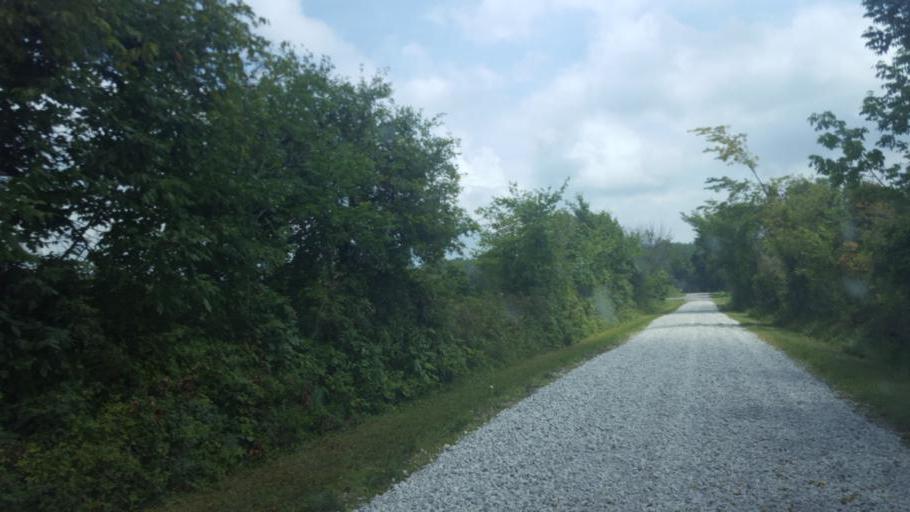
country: US
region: Ohio
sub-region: Morrow County
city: Mount Gilead
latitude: 40.5725
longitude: -82.7024
